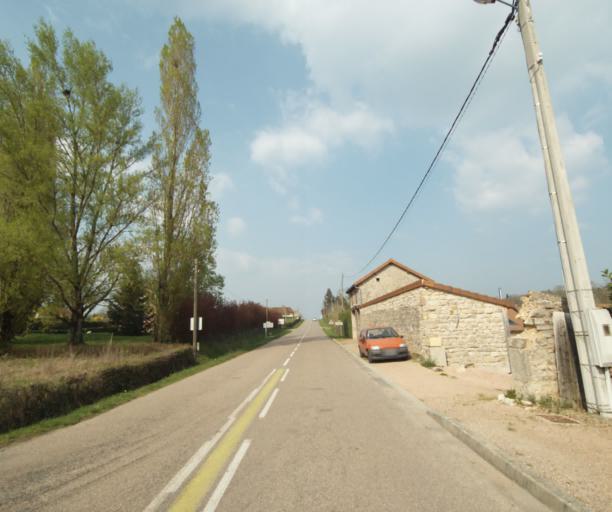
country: FR
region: Bourgogne
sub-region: Departement de Saone-et-Loire
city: Charolles
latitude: 46.4867
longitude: 4.4432
